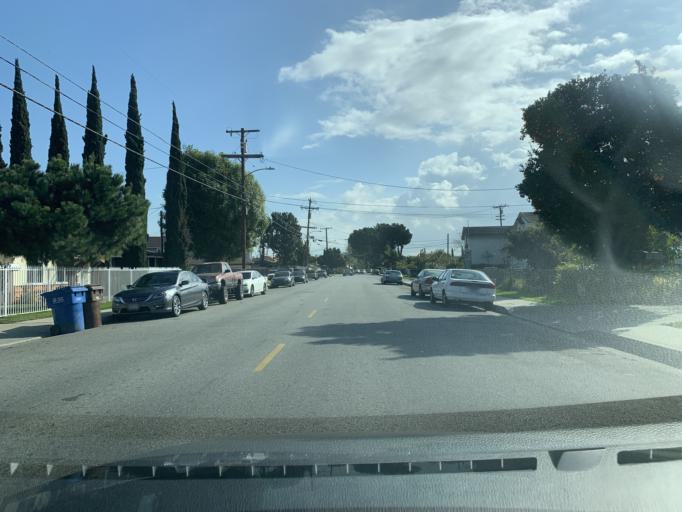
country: US
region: California
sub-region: Los Angeles County
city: South El Monte
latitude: 34.0673
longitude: -118.0567
